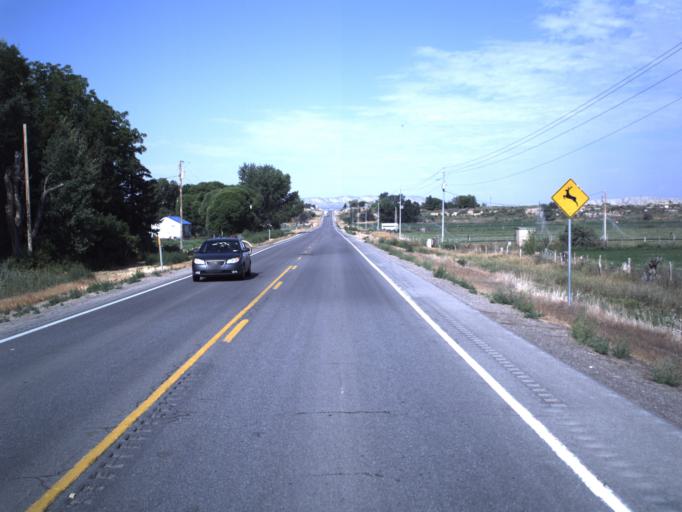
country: US
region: Utah
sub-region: Uintah County
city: Naples
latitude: 40.3695
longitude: -109.3664
